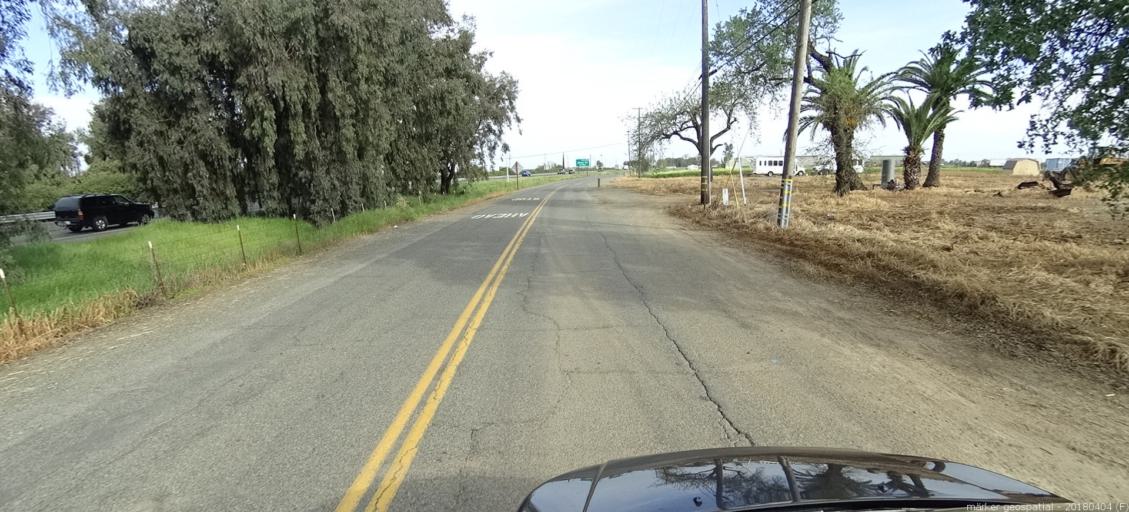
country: US
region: California
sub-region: Sacramento County
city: Galt
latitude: 38.2933
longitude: -121.3130
